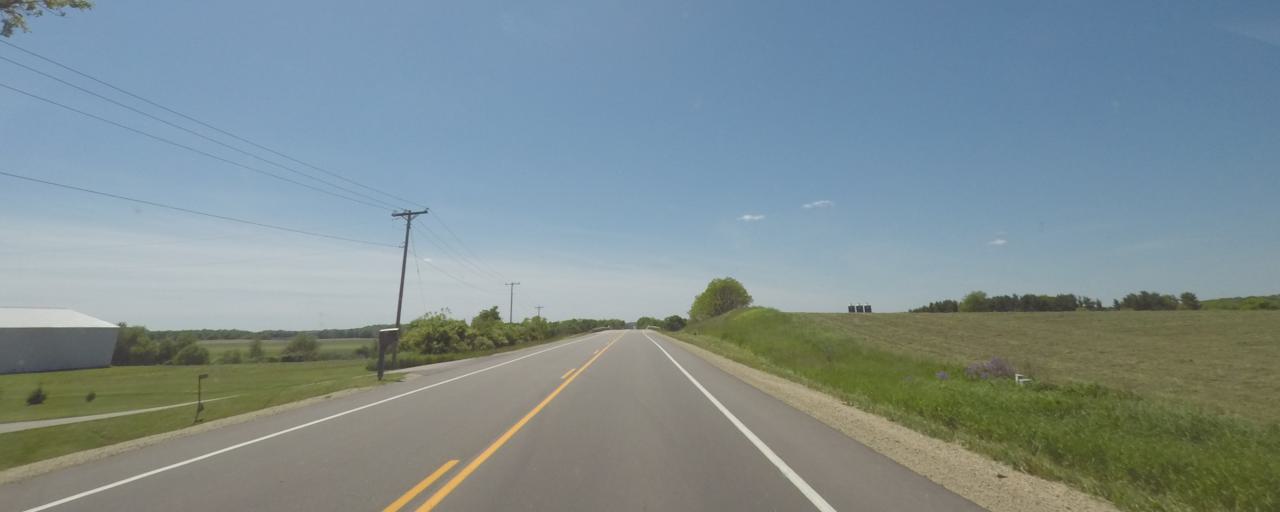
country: US
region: Wisconsin
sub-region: Dane County
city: Oregon
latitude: 42.9502
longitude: -89.3882
